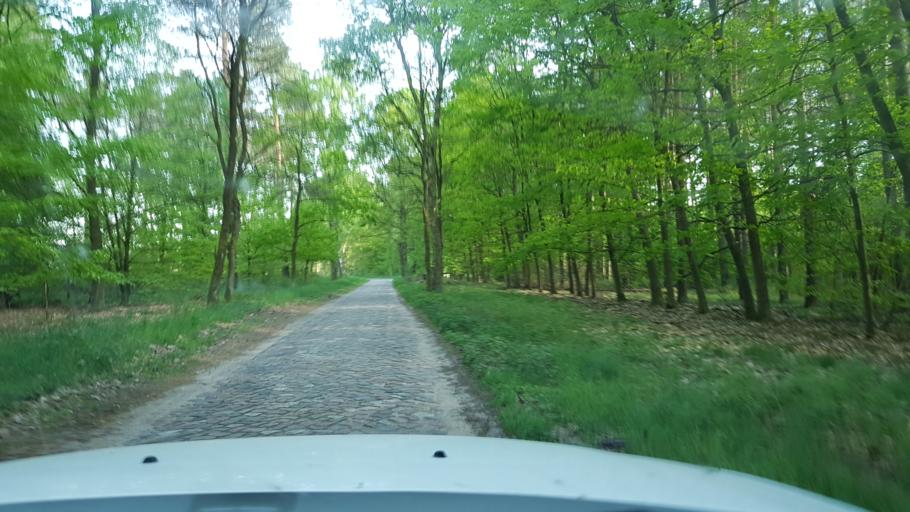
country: PL
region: West Pomeranian Voivodeship
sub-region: Powiat lobeski
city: Resko
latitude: 53.7199
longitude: 15.3297
